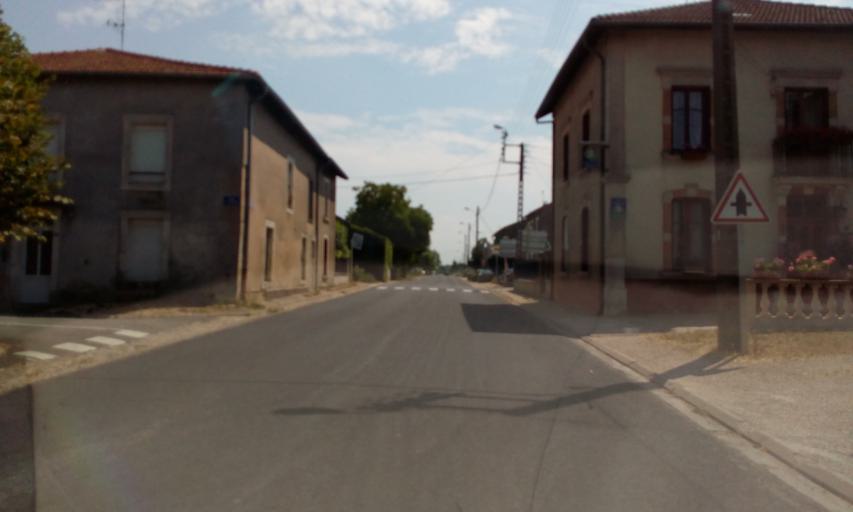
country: FR
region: Lorraine
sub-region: Departement de la Meuse
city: Vigneulles-les-Hattonchatel
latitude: 49.0385
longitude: 5.6580
